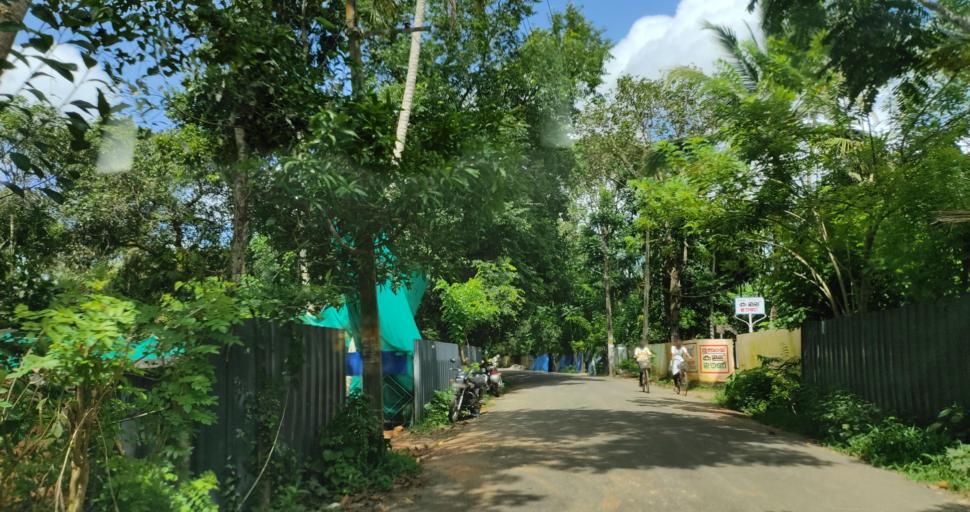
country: IN
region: Kerala
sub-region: Alappuzha
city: Shertallai
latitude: 9.6640
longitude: 76.3786
